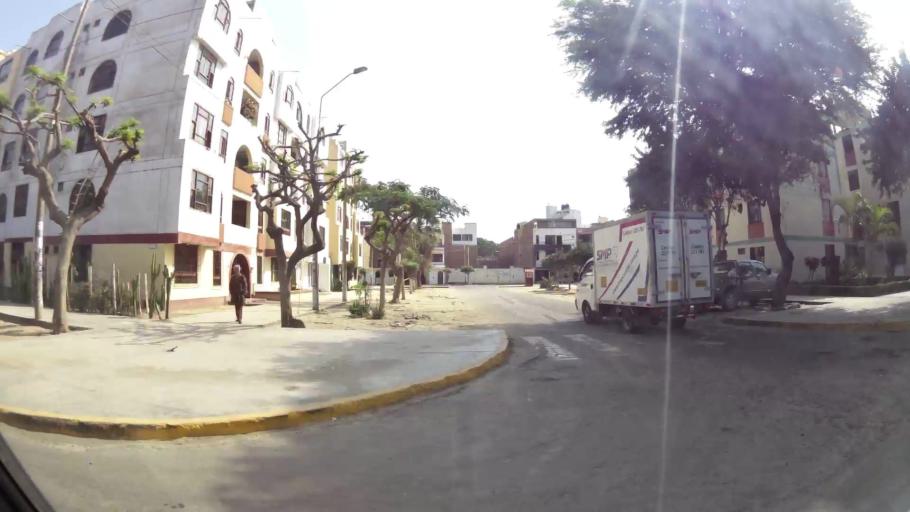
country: PE
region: La Libertad
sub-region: Provincia de Trujillo
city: Trujillo
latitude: -8.1213
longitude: -79.0399
